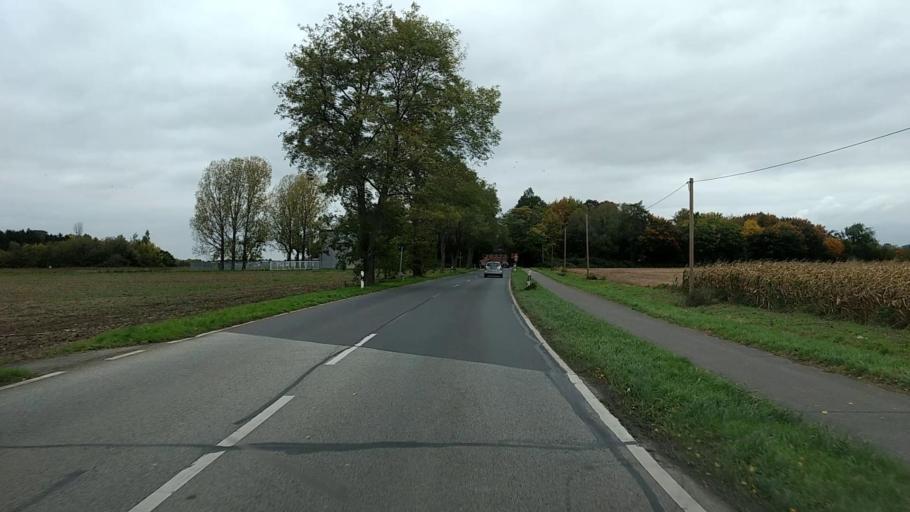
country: DE
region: North Rhine-Westphalia
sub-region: Regierungsbezirk Koln
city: Bergheim
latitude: 50.9148
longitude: 6.6676
